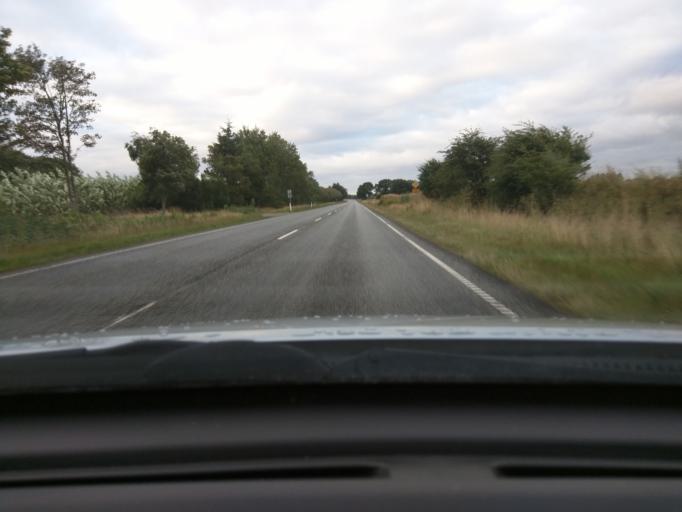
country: DK
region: Central Jutland
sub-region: Silkeborg Kommune
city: Kjellerup
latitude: 56.3163
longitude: 9.3298
